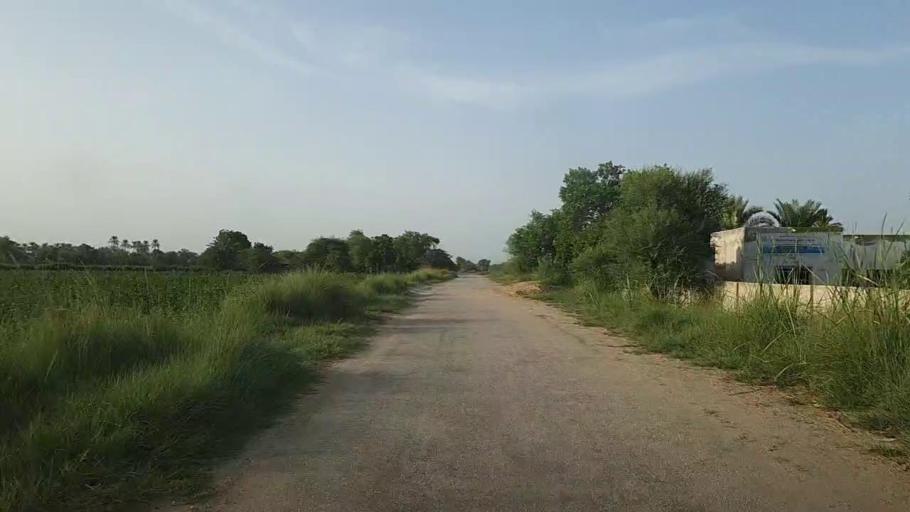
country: PK
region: Sindh
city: Bhiria
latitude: 26.8972
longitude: 68.2626
